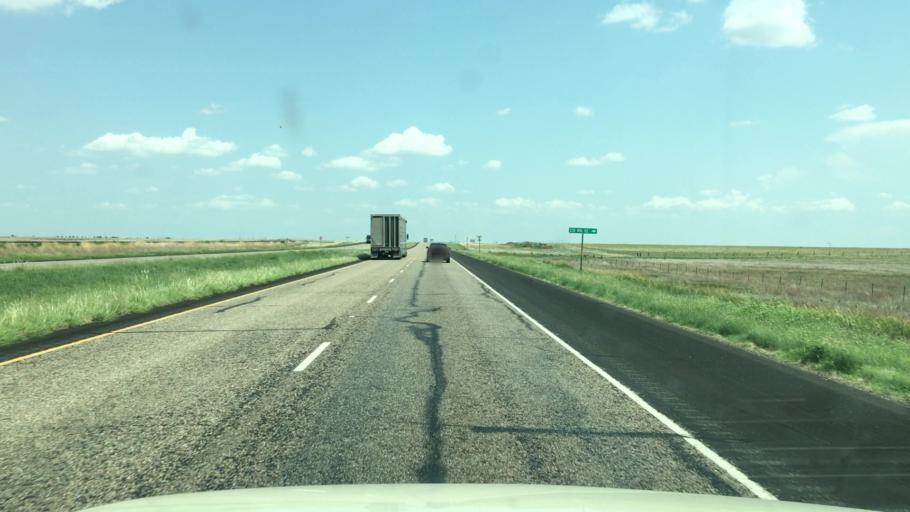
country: US
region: Texas
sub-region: Armstrong County
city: Claude
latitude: 35.1319
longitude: -101.4190
